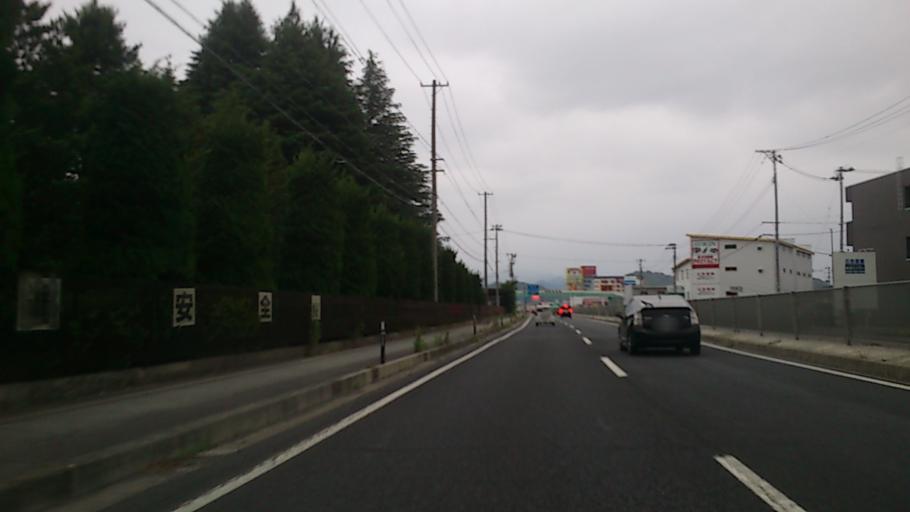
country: JP
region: Yamagata
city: Tendo
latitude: 38.3794
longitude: 140.3825
